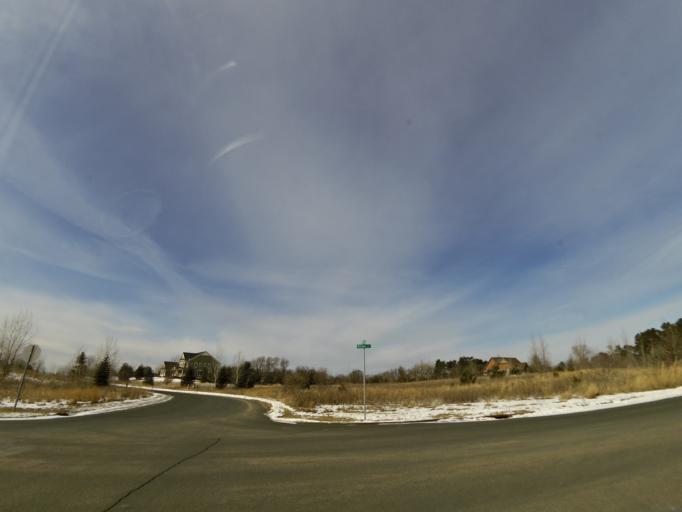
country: US
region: Minnesota
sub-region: Washington County
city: Lake Elmo
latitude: 44.9801
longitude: -92.8508
